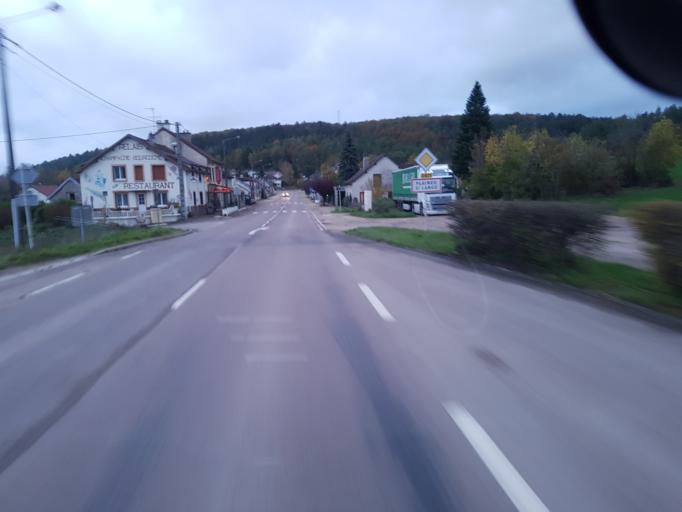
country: FR
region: Champagne-Ardenne
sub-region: Departement de l'Aube
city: Mussy-sur-Seine
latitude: 47.9938
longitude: 4.4832
